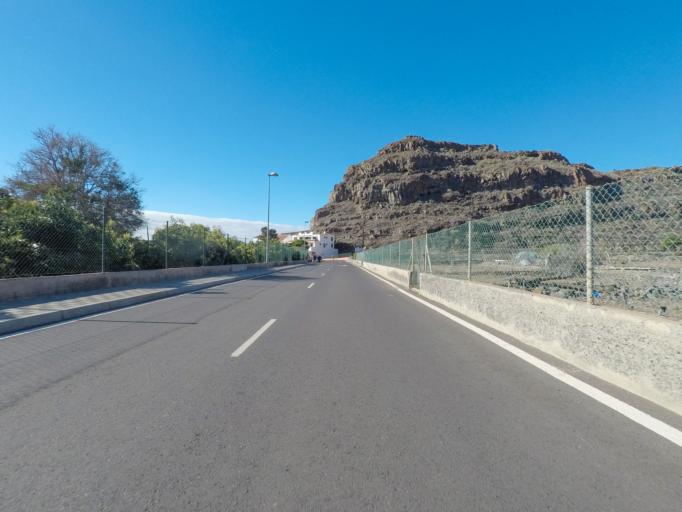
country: ES
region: Canary Islands
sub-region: Provincia de Santa Cruz de Tenerife
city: Alajero
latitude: 28.0309
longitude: -17.1942
